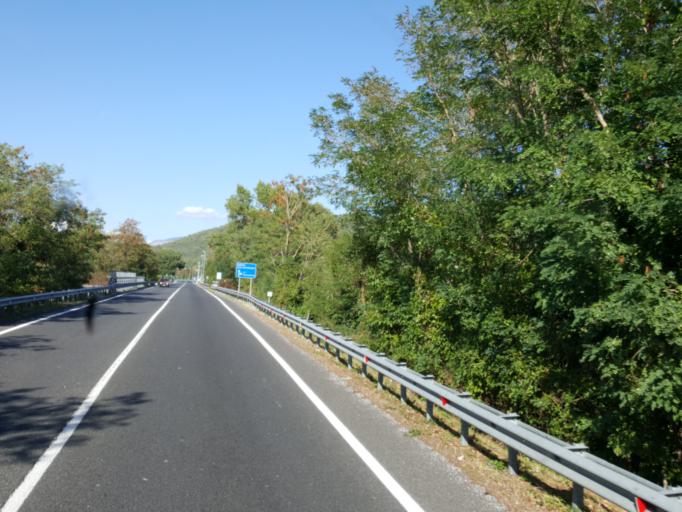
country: IT
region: Molise
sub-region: Provincia di Isernia
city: Taverna Ravindola
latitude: 41.5270
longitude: 14.1502
